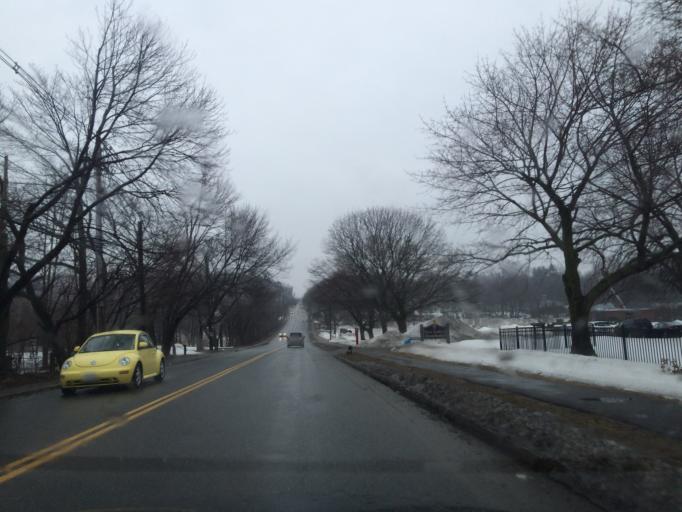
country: US
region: Massachusetts
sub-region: Middlesex County
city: Waltham
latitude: 42.4096
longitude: -71.2297
